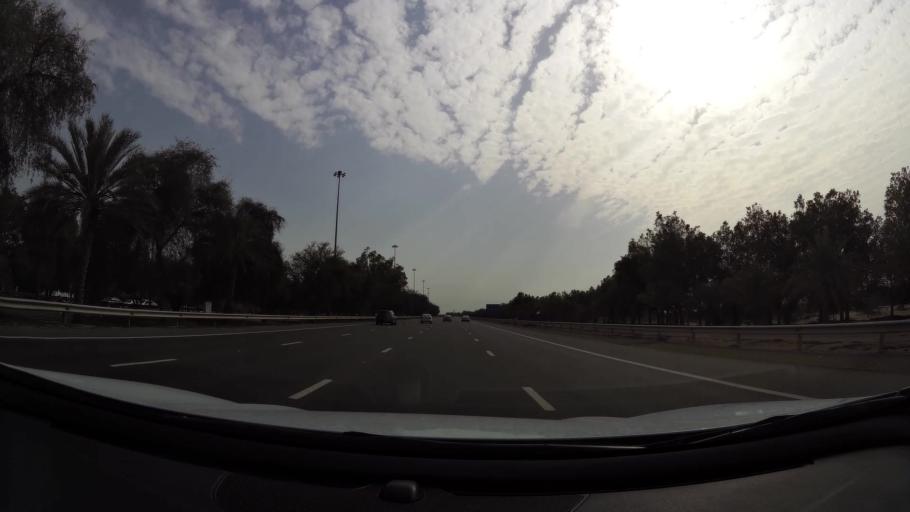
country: AE
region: Abu Dhabi
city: Abu Dhabi
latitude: 24.4925
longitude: 54.6779
